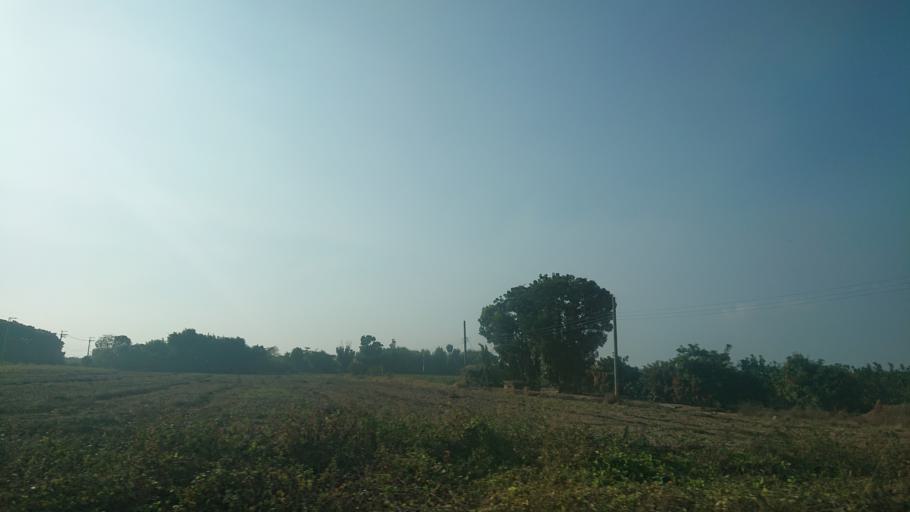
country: TW
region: Taiwan
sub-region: Tainan
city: Tainan
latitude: 23.1466
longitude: 120.2469
